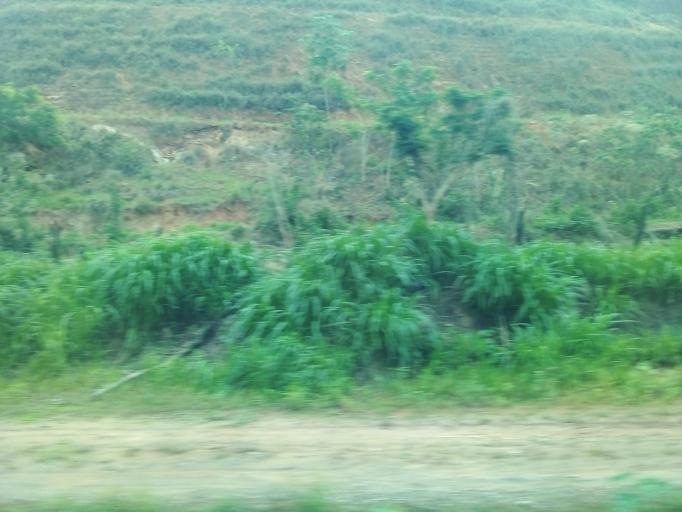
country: BR
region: Minas Gerais
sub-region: Governador Valadares
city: Governador Valadares
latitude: -19.0722
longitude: -42.1524
